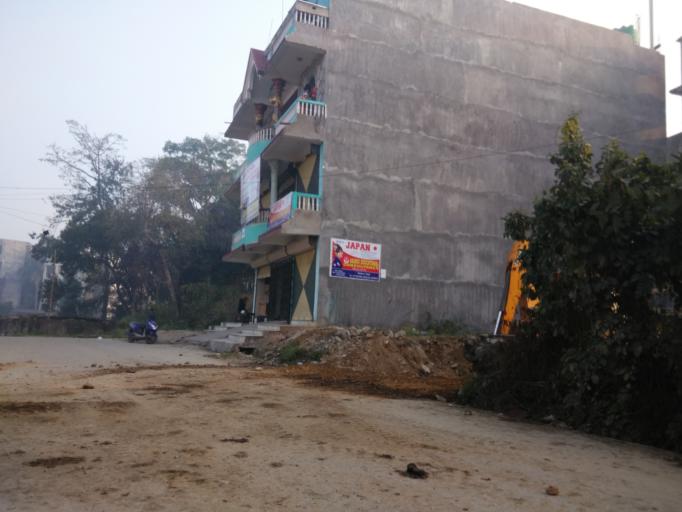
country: NP
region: Central Region
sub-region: Narayani Zone
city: Bharatpur
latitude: 27.6931
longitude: 84.4265
